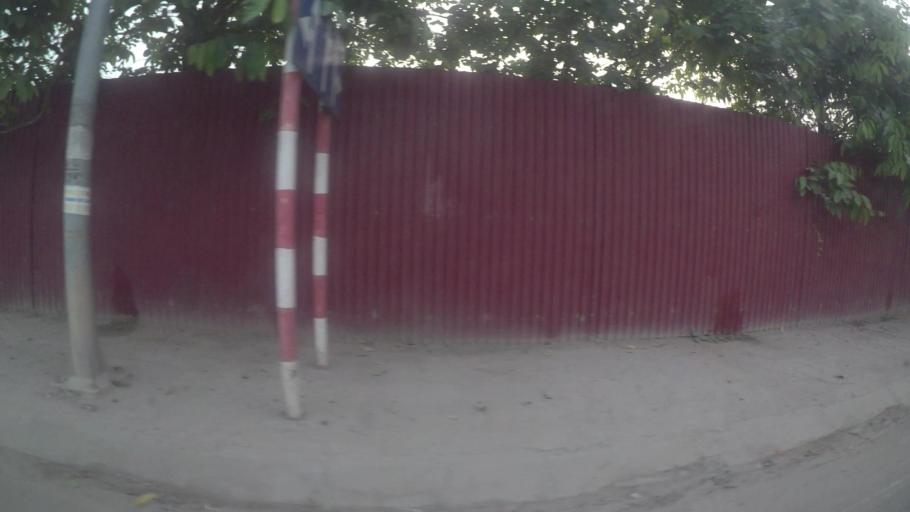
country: VN
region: Ha Noi
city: Ha Dong
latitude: 20.9939
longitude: 105.7355
